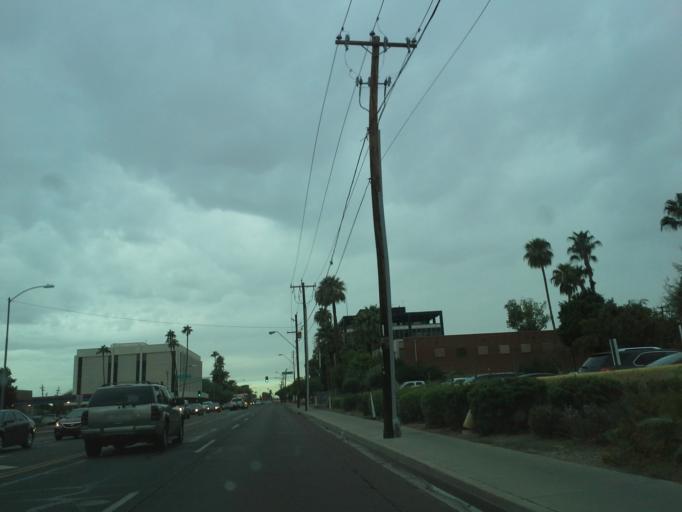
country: US
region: Arizona
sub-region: Maricopa County
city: Phoenix
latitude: 33.4876
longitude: -112.0768
